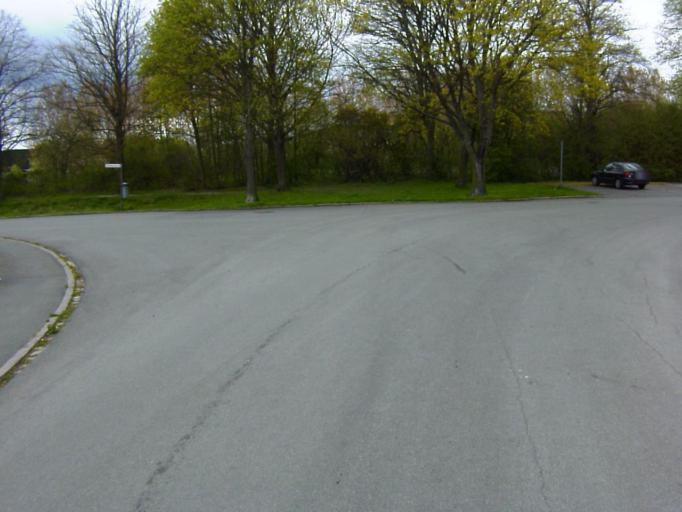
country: SE
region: Skane
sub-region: Kristianstads Kommun
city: Kristianstad
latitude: 56.0452
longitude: 14.1634
